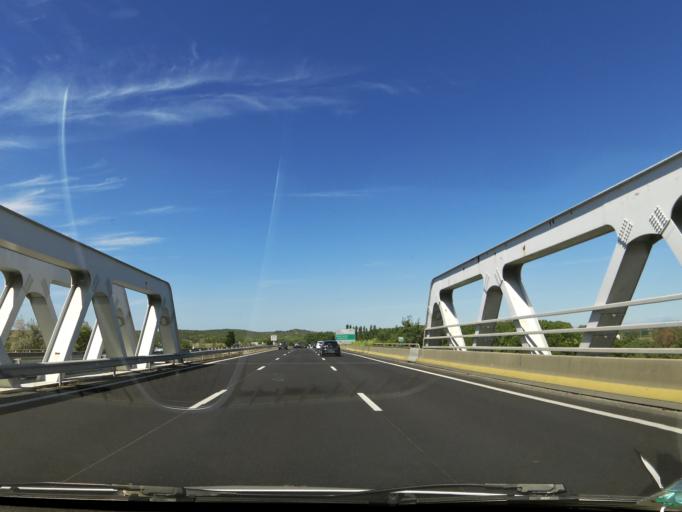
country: FR
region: Languedoc-Roussillon
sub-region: Departement du Gard
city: Rodilhan
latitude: 43.8447
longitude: 4.4167
